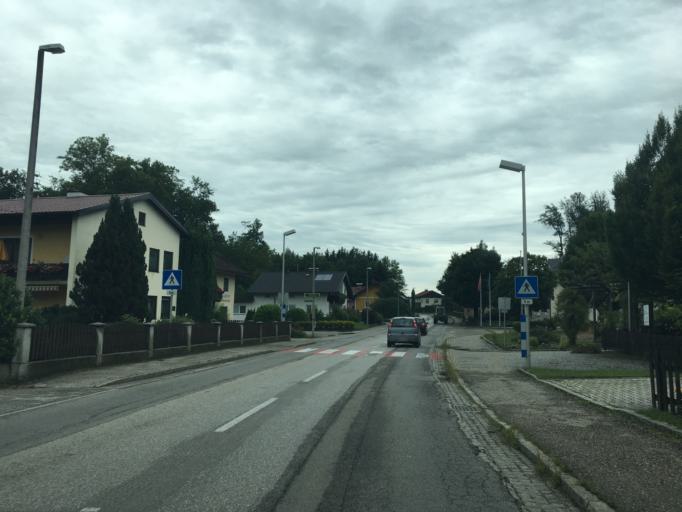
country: AT
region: Salzburg
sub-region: Politischer Bezirk Salzburg-Umgebung
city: Dorfbeuern
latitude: 48.0469
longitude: 12.9883
